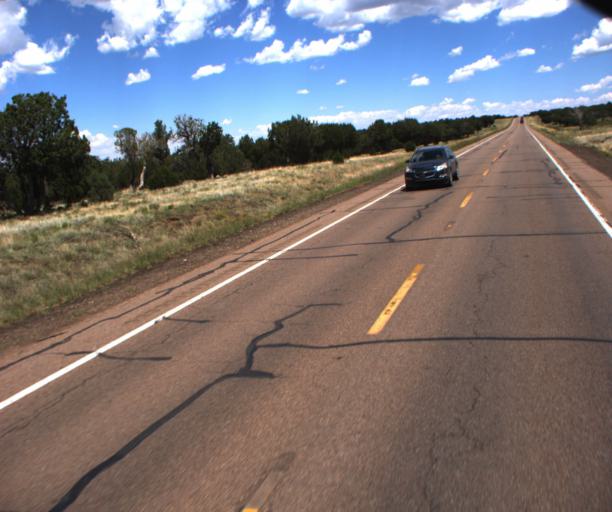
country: US
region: Arizona
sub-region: Navajo County
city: Show Low
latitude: 34.2699
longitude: -109.9288
